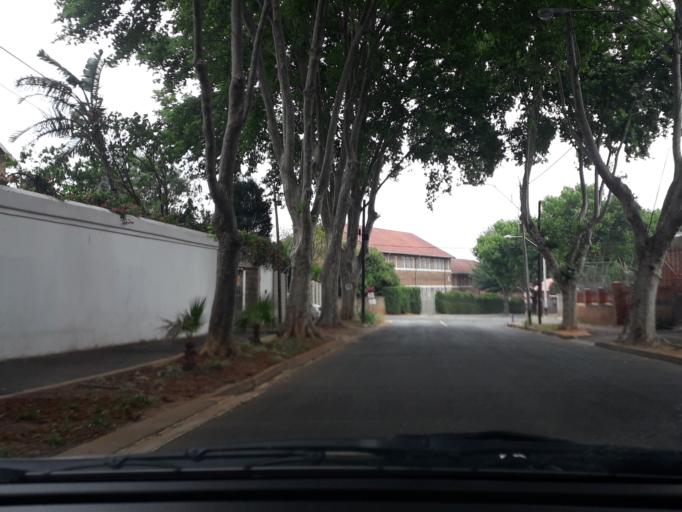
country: ZA
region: Gauteng
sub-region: City of Johannesburg Metropolitan Municipality
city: Johannesburg
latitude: -26.1534
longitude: 28.0890
